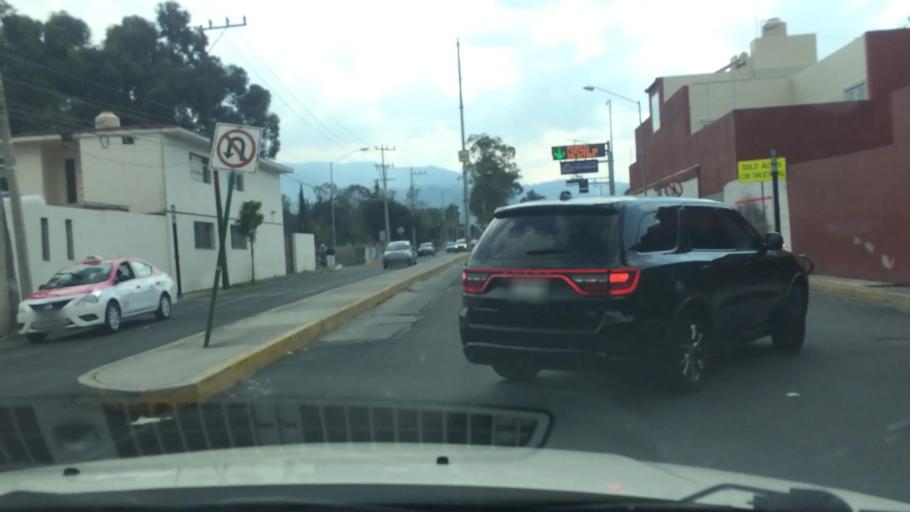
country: MX
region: Mexico City
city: Magdalena Contreras
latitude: 19.3454
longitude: -99.2385
